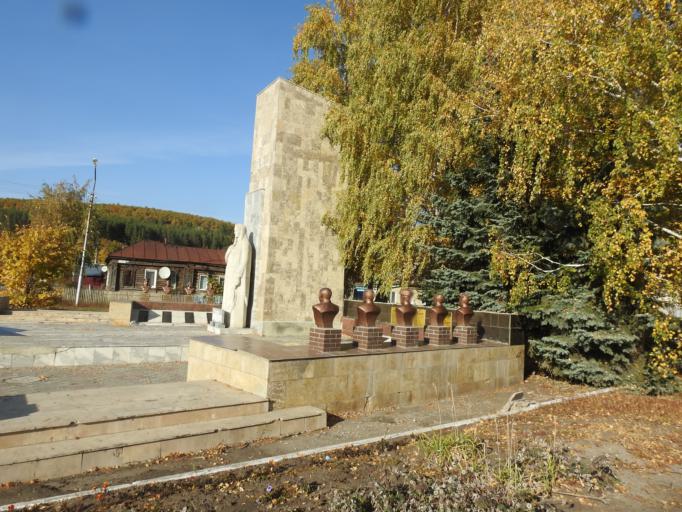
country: RU
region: Saratov
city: Baltay
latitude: 52.4678
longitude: 46.6300
